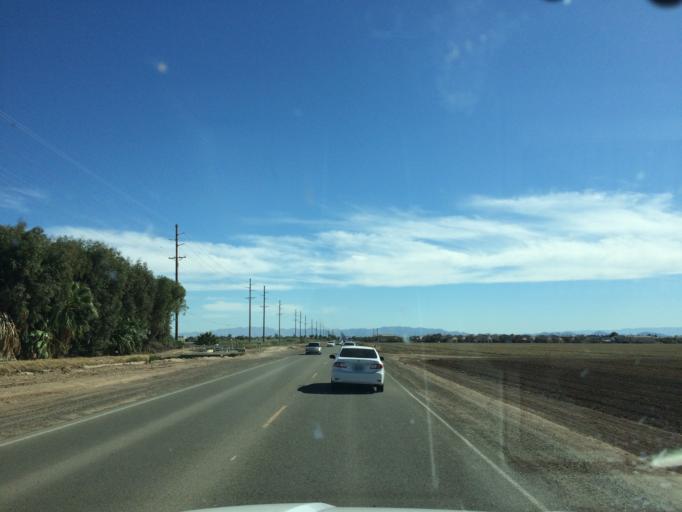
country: US
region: California
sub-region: Imperial County
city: Heber
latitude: 32.7458
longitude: -115.5346
